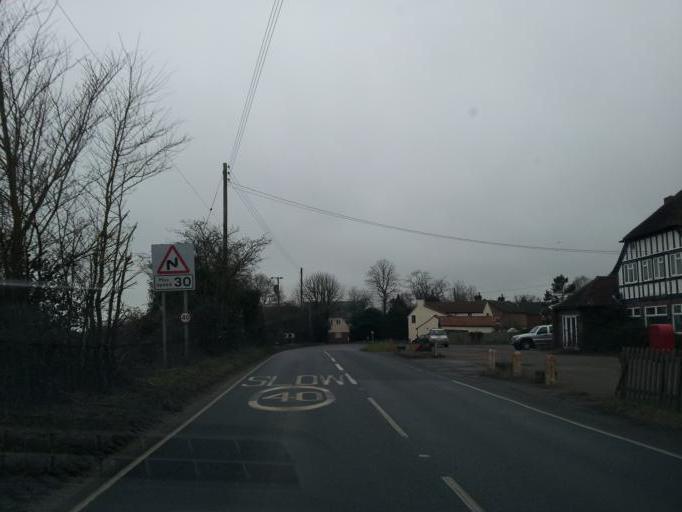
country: GB
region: England
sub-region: Essex
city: Mistley
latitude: 51.9155
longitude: 1.0867
